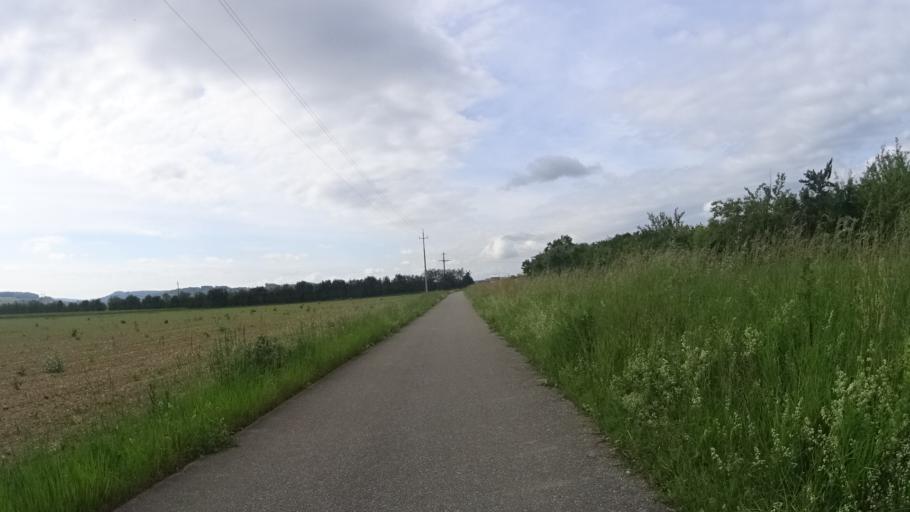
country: DE
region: Baden-Wuerttemberg
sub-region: Freiburg Region
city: Schliengen
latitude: 47.7803
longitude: 7.5540
